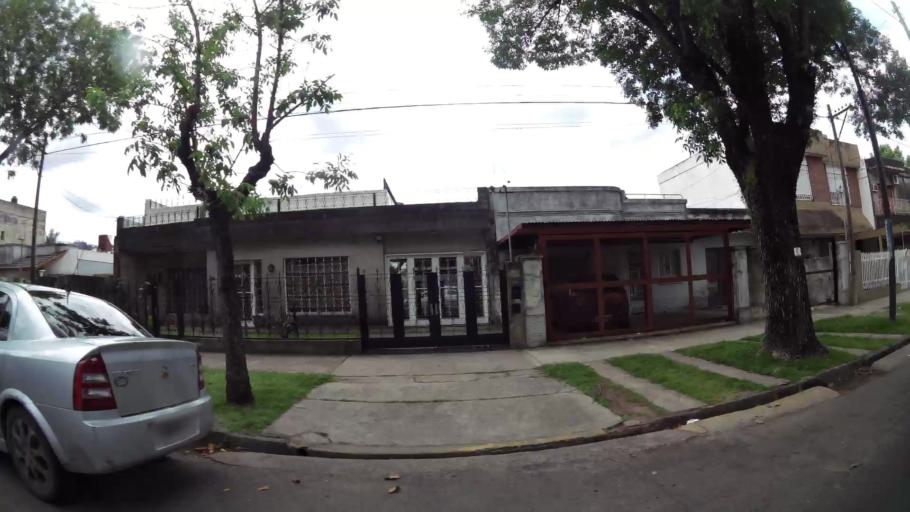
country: AR
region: Santa Fe
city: Gobernador Galvez
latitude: -32.9996
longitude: -60.6408
